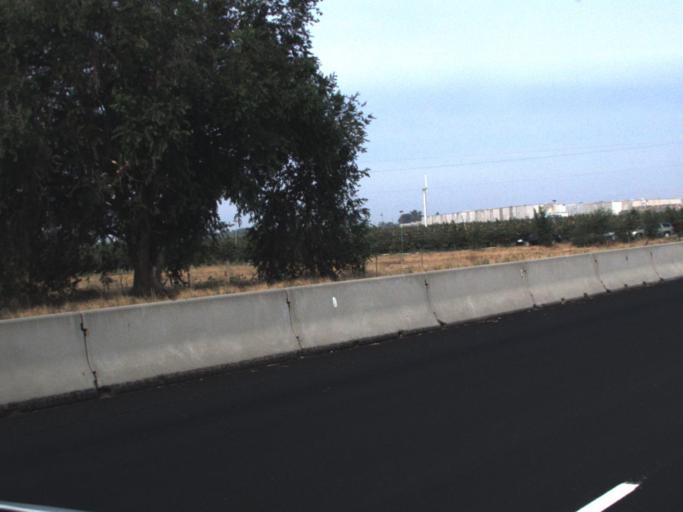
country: US
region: Washington
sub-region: Yakima County
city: Wapato
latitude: 46.4355
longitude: -120.4213
